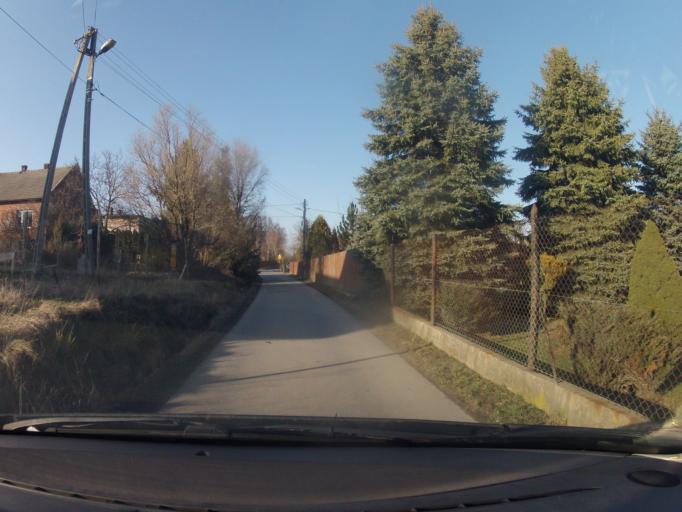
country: PL
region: Lesser Poland Voivodeship
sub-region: Powiat wielicki
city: Wieliczka
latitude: 49.9895
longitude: 20.0206
